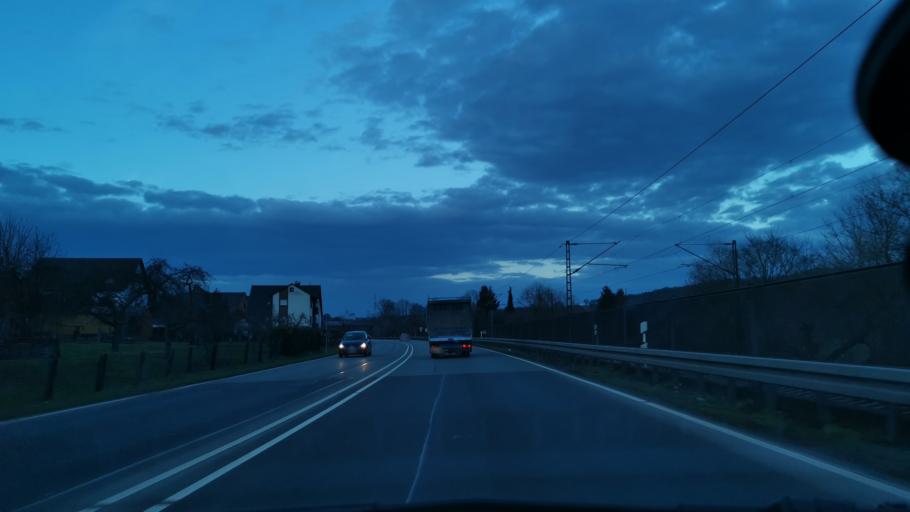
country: DE
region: Hesse
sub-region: Regierungsbezirk Kassel
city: Bad Hersfeld
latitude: 50.8996
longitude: 9.7471
